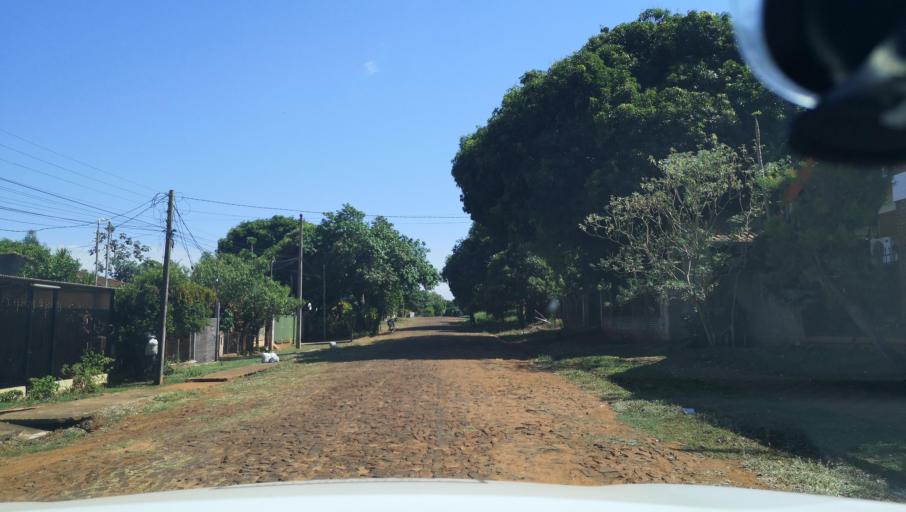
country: PY
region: Itapua
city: Carmen del Parana
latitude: -27.1650
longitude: -56.2314
